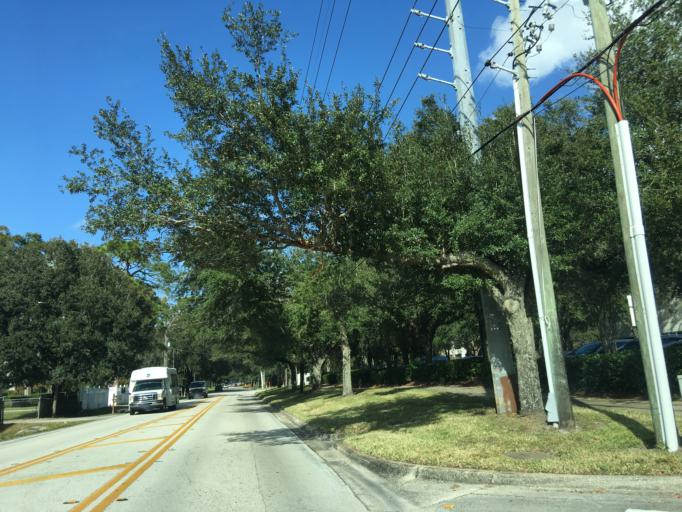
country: US
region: Florida
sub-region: Orange County
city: Eatonville
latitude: 28.6204
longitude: -81.3982
